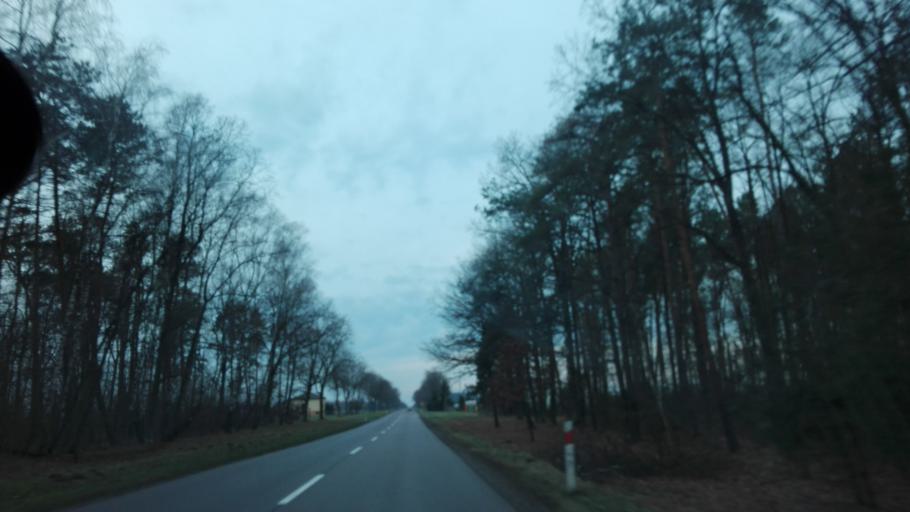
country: PL
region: Lublin Voivodeship
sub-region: Powiat radzynski
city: Radzyn Podlaski
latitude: 51.7768
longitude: 22.6630
